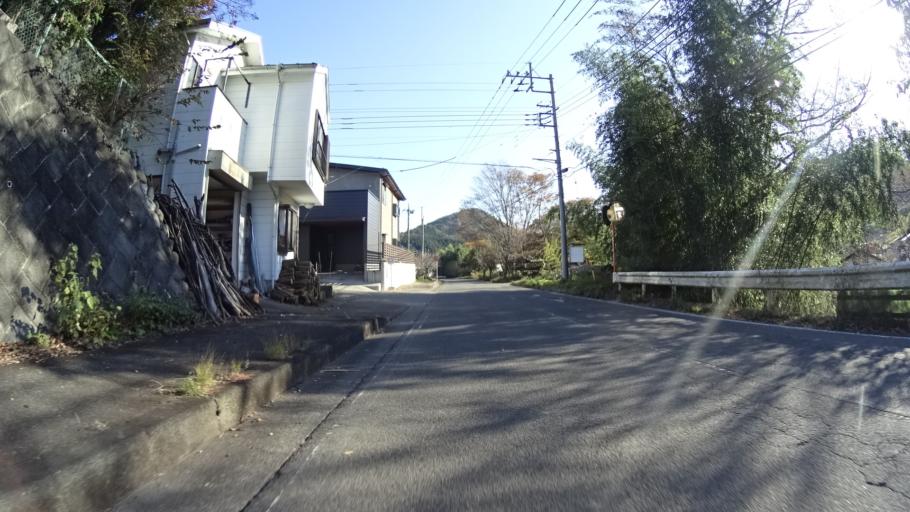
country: JP
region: Yamanashi
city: Uenohara
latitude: 35.6456
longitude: 139.1253
